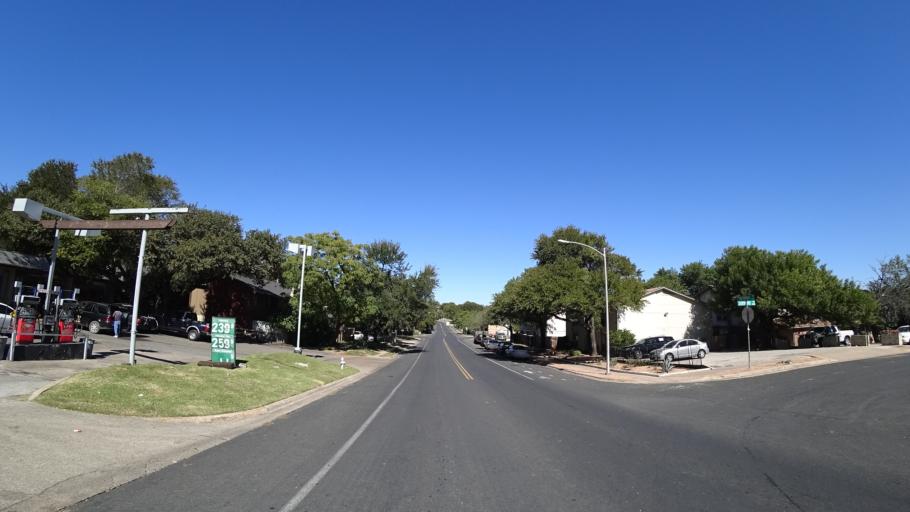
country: US
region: Texas
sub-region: Travis County
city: Rollingwood
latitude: 30.2319
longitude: -97.7774
